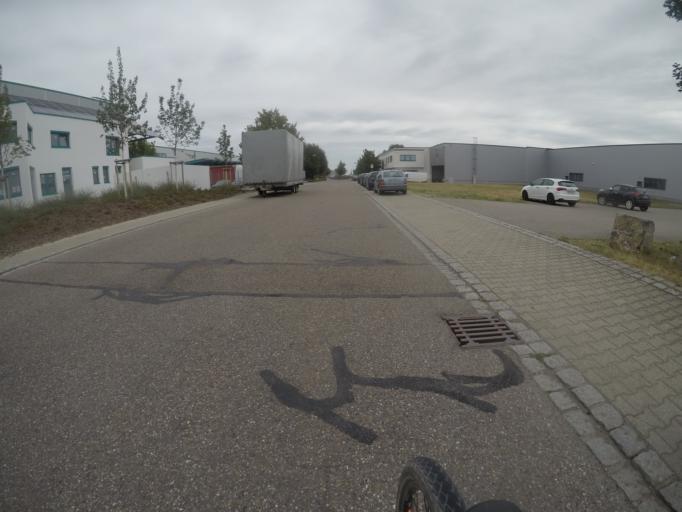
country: DE
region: Baden-Wuerttemberg
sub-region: Karlsruhe Region
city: Illingen
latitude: 48.9516
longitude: 8.8825
